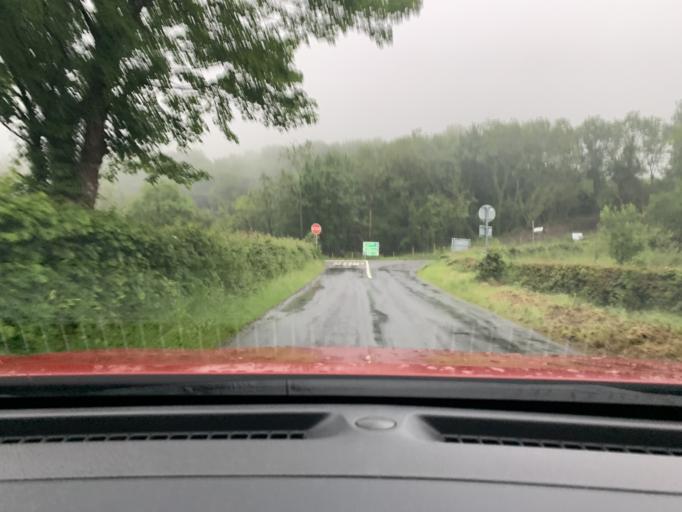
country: IE
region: Connaught
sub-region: Sligo
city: Sligo
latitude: 54.3230
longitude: -8.4244
